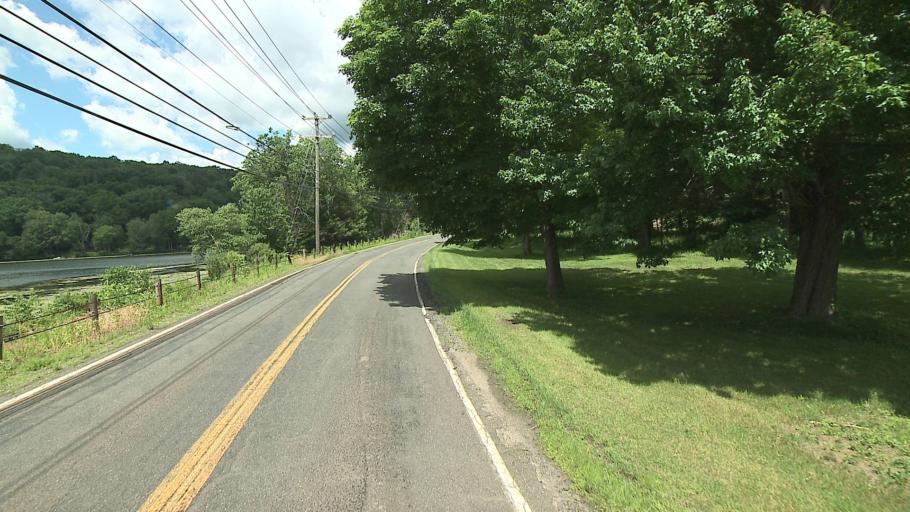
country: US
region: Connecticut
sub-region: Litchfield County
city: Kent
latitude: 41.6861
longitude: -73.4787
